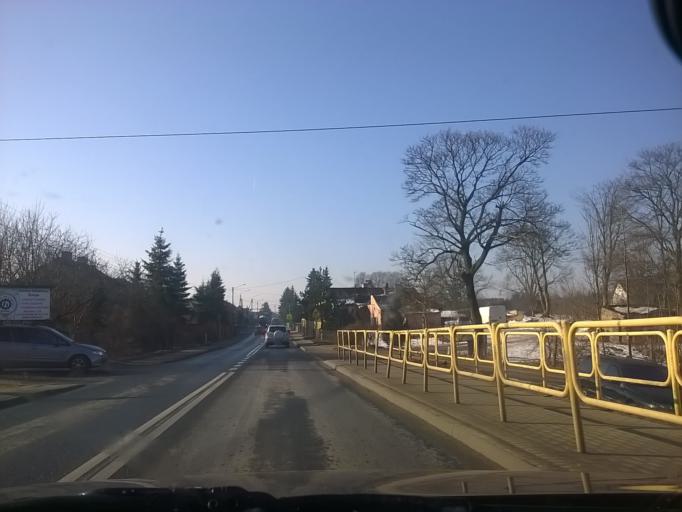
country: PL
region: Warmian-Masurian Voivodeship
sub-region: Powiat mragowski
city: Mragowo
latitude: 53.8596
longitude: 21.2747
